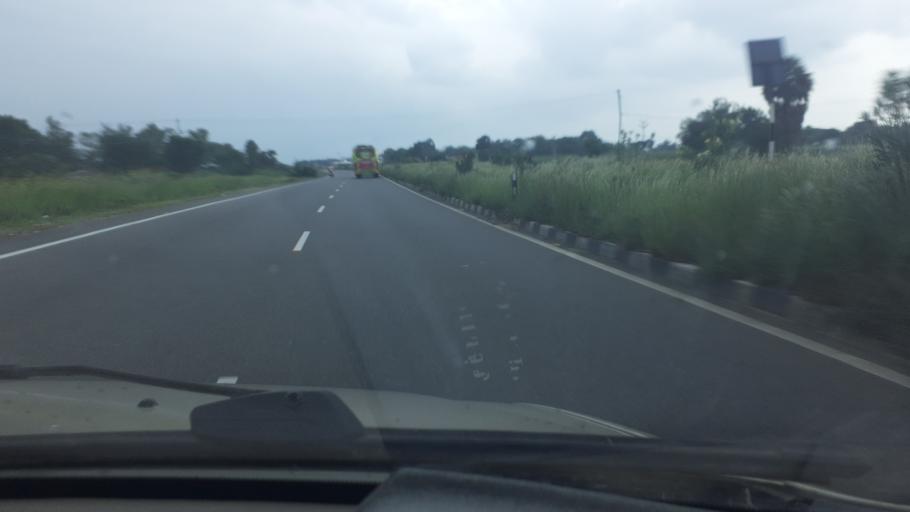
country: IN
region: Tamil Nadu
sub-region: Virudhunagar
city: Virudunagar
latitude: 9.6813
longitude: 77.9686
